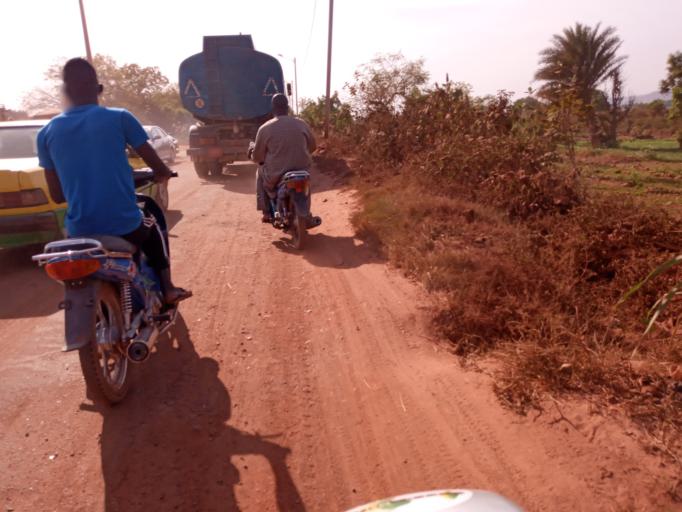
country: ML
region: Bamako
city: Bamako
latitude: 12.6360
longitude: -7.9278
